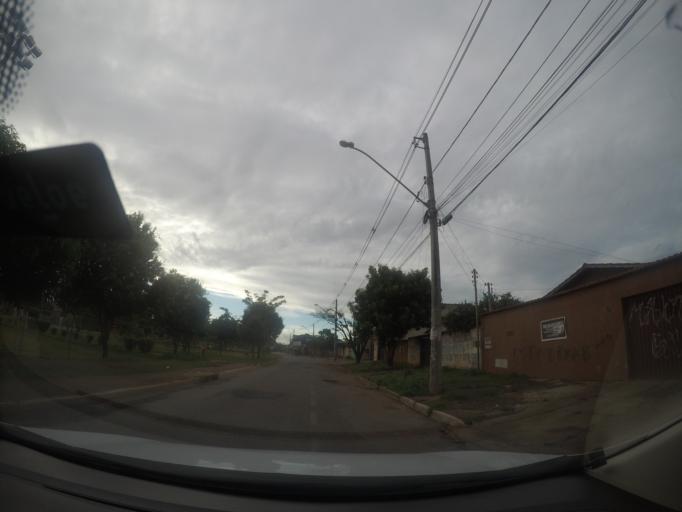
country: BR
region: Goias
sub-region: Goiania
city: Goiania
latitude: -16.6149
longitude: -49.3419
